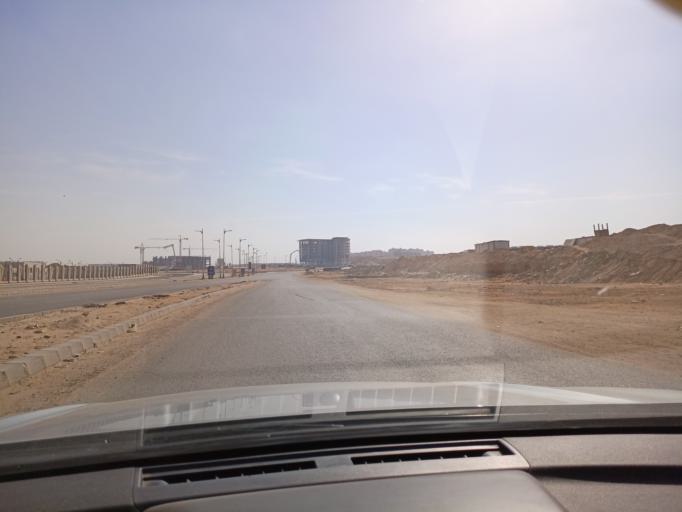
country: EG
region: Muhafazat al Qalyubiyah
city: Al Khankah
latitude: 30.0413
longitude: 31.6856
